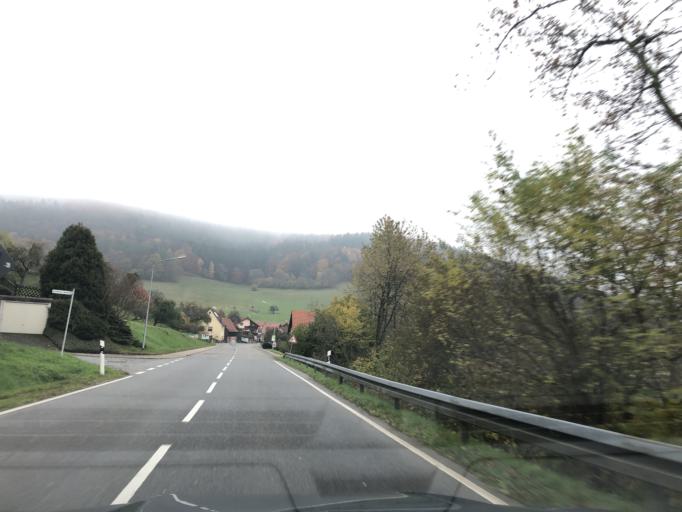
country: DE
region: Hesse
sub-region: Regierungsbezirk Darmstadt
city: Wald-Michelbach
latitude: 49.5404
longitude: 8.8608
